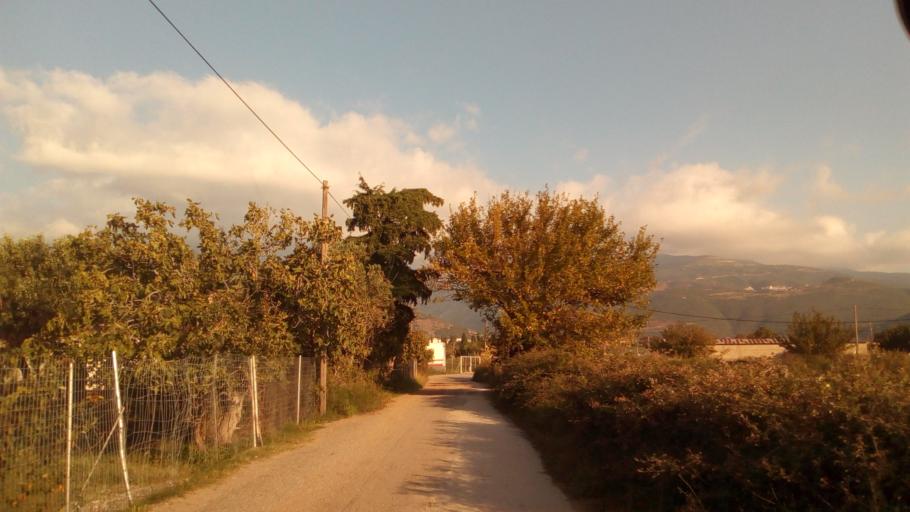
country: GR
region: West Greece
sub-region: Nomos Aitolias kai Akarnanias
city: Nafpaktos
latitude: 38.3864
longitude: 21.8497
